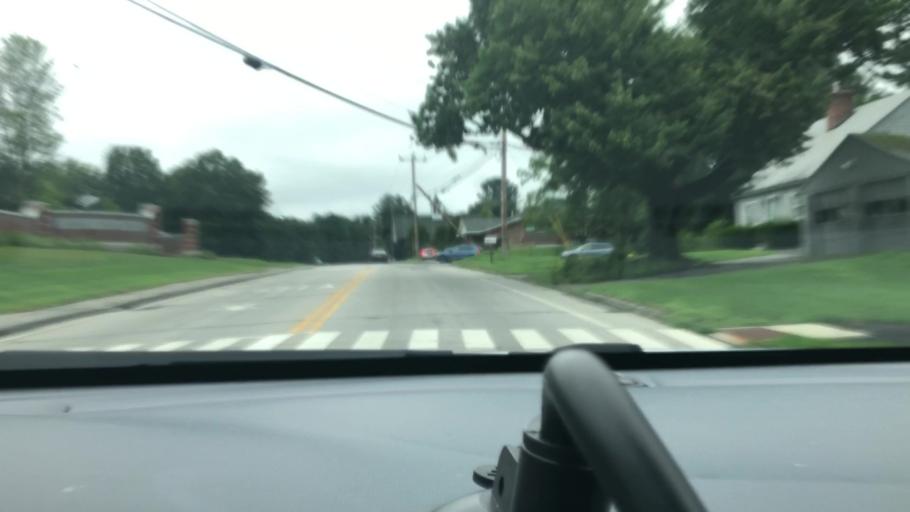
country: US
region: New Hampshire
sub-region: Hillsborough County
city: Pinardville
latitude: 42.9876
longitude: -71.5053
